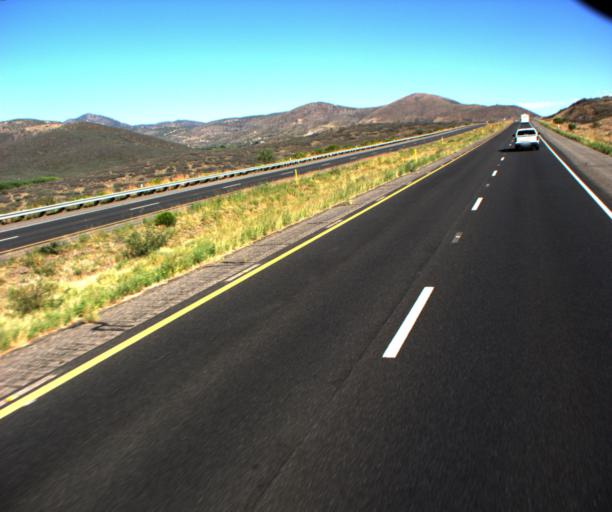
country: US
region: Arizona
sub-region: Yavapai County
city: Mayer
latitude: 34.4385
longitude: -112.2624
